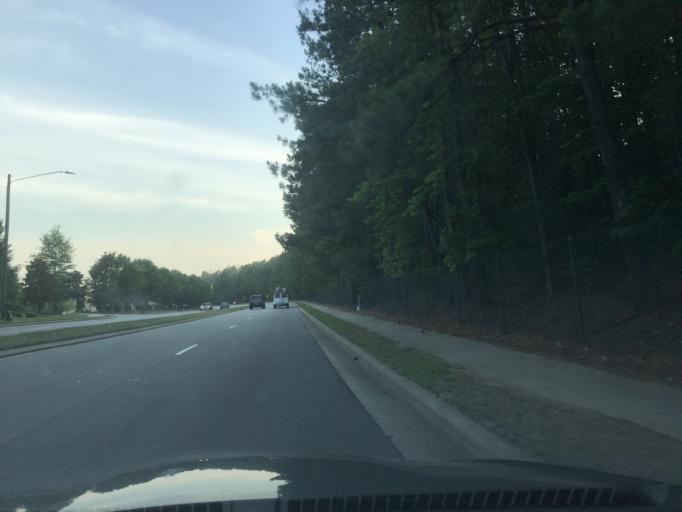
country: US
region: North Carolina
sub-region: Wake County
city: Raleigh
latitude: 35.7738
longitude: -78.6137
